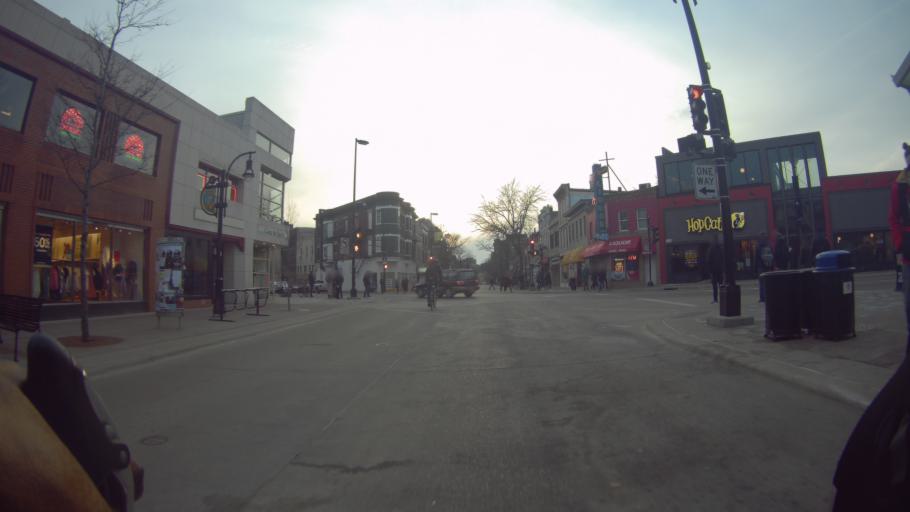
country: US
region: Wisconsin
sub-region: Dane County
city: Madison
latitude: 43.0748
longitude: -89.3915
